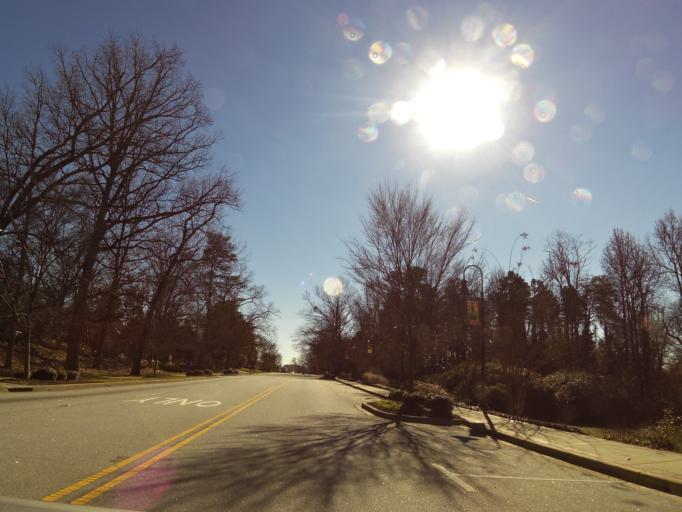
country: US
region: South Carolina
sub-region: Greenville County
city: Travelers Rest
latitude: 34.9604
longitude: -82.4402
